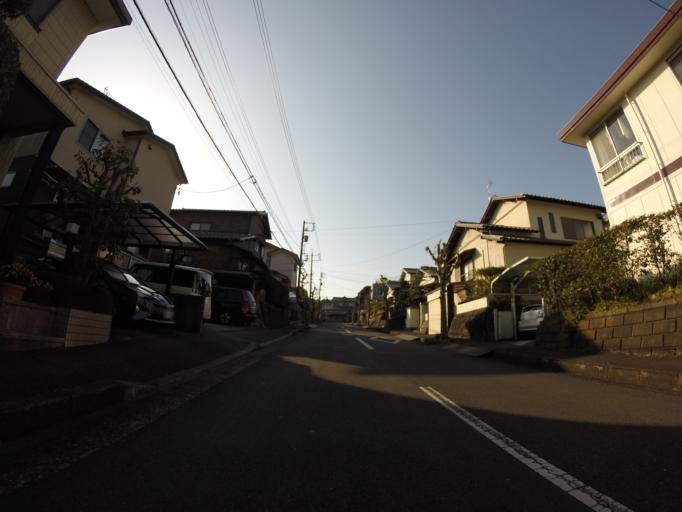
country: JP
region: Shizuoka
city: Shizuoka-shi
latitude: 34.9913
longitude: 138.4540
